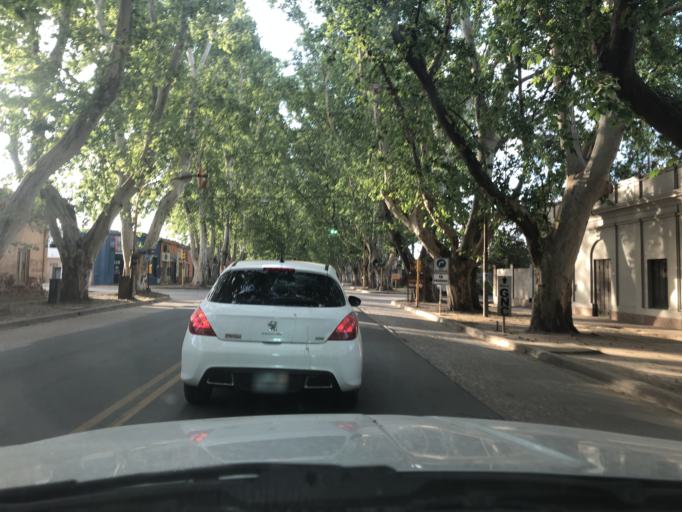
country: AR
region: Cordoba
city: Jesus Maria
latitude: -30.9962
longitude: -64.0911
